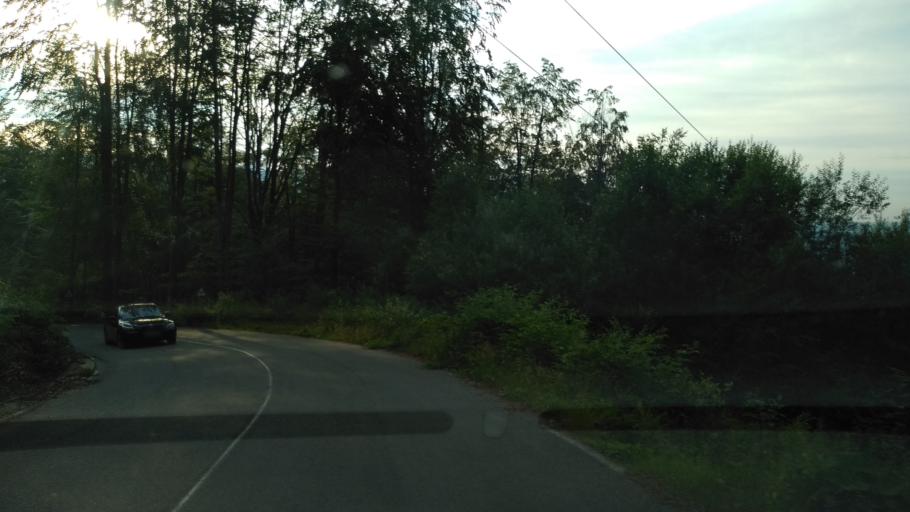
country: RO
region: Hunedoara
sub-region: Municipiul  Vulcan
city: Jiu-Paroseni
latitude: 45.3375
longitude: 23.2914
